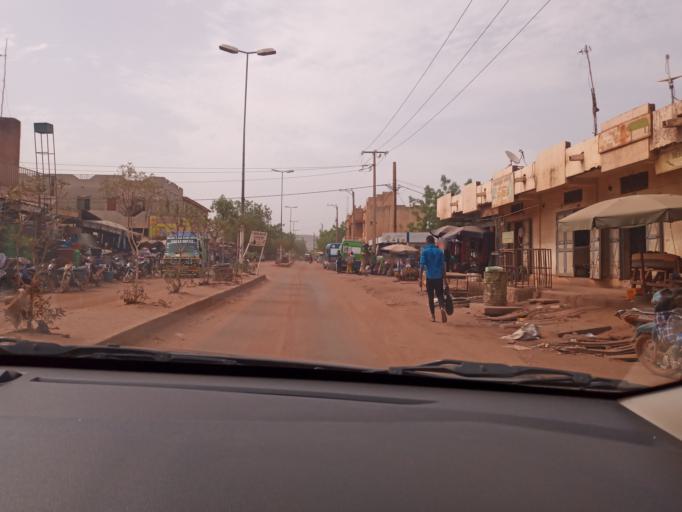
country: ML
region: Bamako
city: Bamako
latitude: 12.6750
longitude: -7.9242
